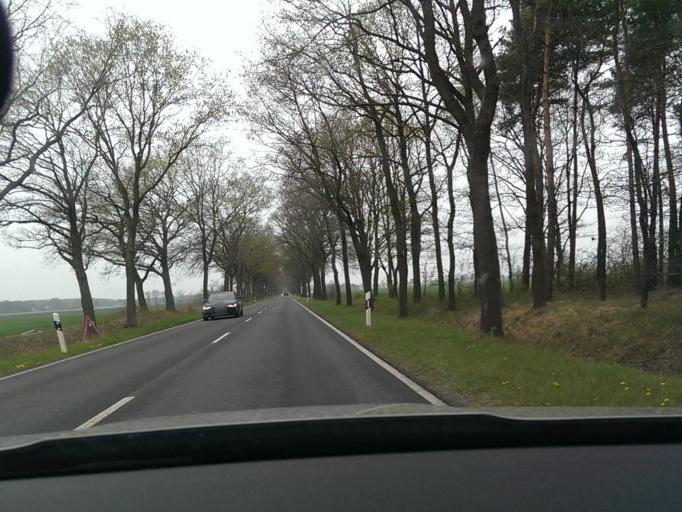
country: DE
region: Lower Saxony
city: Essel
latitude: 52.6551
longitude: 9.6719
